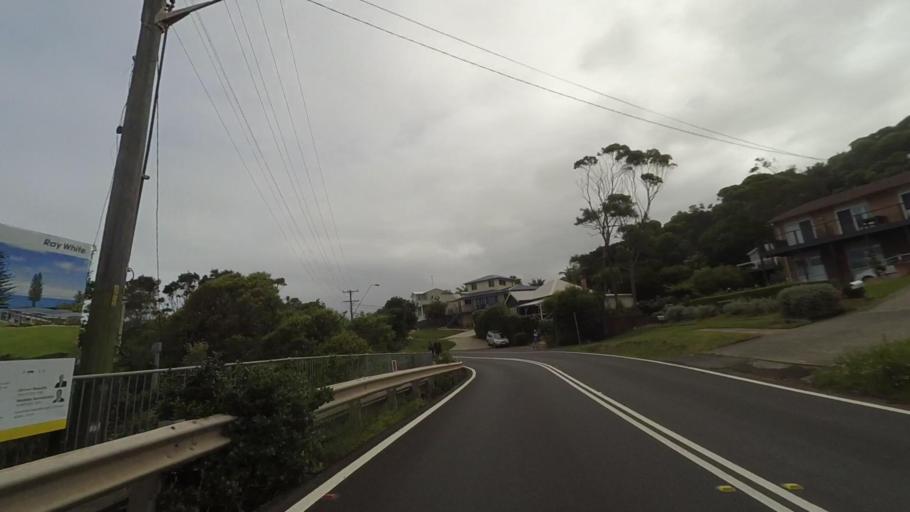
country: AU
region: New South Wales
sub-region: Wollongong
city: Bulli
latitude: -34.2820
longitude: 150.9528
